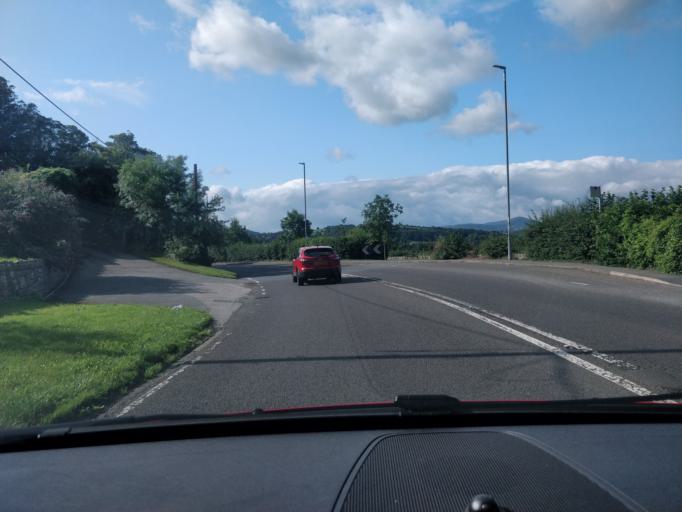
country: GB
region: Wales
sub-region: Conwy
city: Llansantffraid Glan Conwy
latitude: 53.2736
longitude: -3.7966
